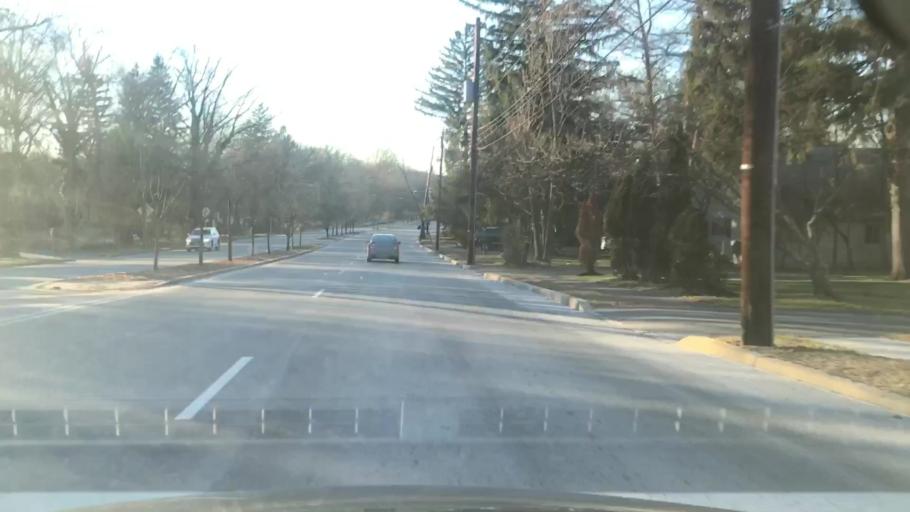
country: US
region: New Jersey
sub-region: Essex County
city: Northfield
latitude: 40.7718
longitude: -74.3104
